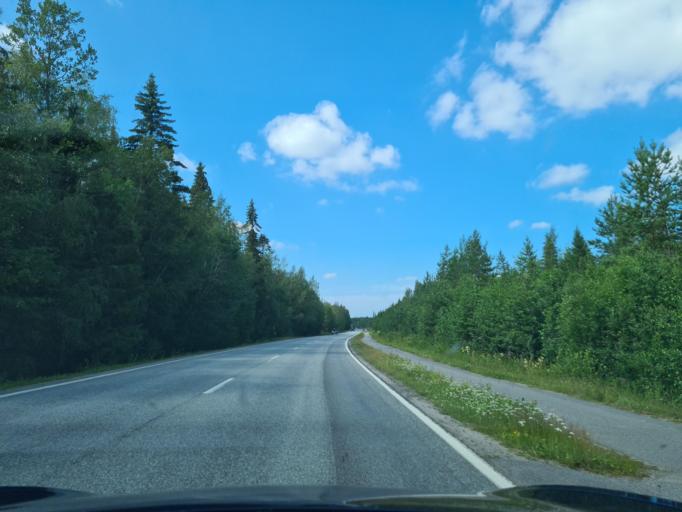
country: FI
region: Ostrobothnia
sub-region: Vaasa
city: Replot
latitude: 63.1996
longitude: 21.5359
